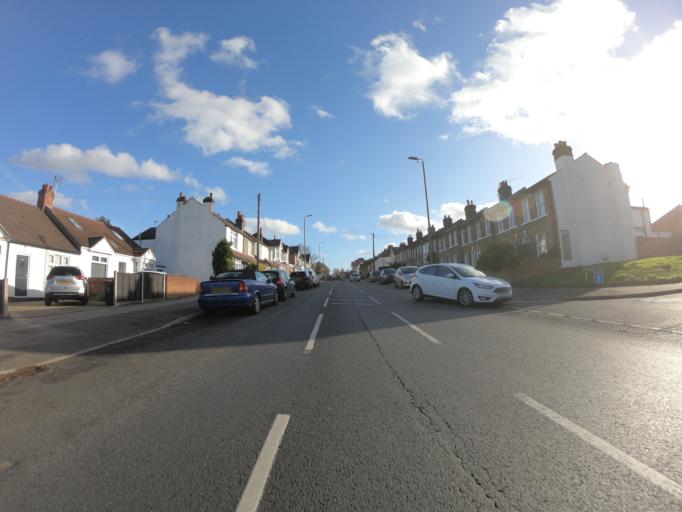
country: GB
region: England
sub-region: Greater London
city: Chislehurst
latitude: 51.4237
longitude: 0.0598
